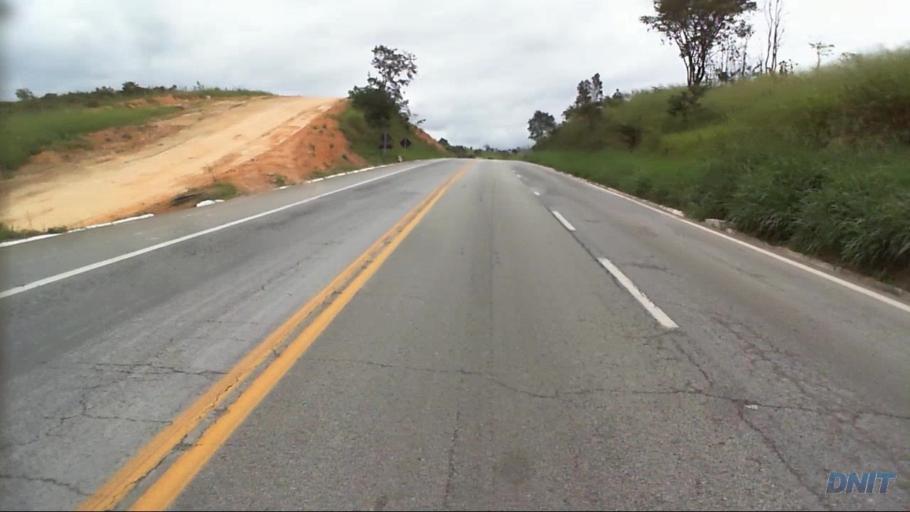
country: BR
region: Minas Gerais
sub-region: Barao De Cocais
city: Barao de Cocais
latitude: -19.7850
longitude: -43.4318
